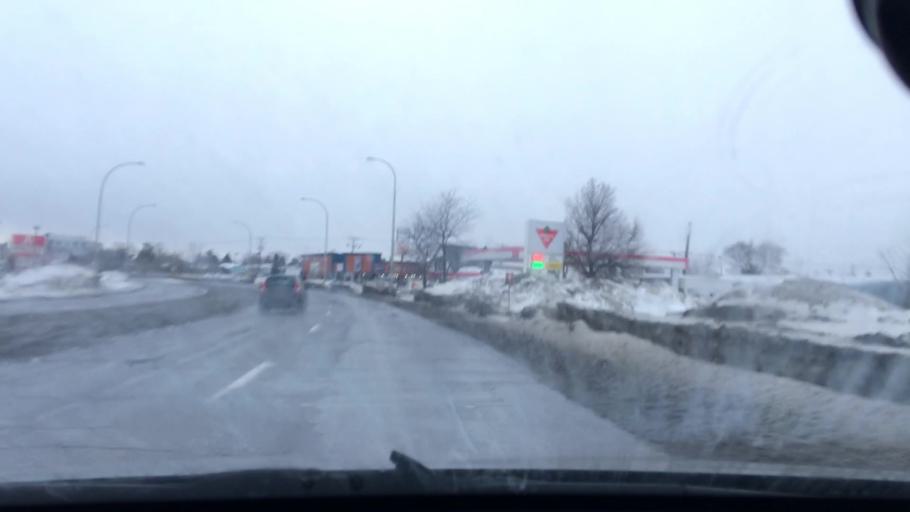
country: CA
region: Quebec
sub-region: Outaouais
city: Gatineau
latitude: 45.4844
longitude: -75.6642
